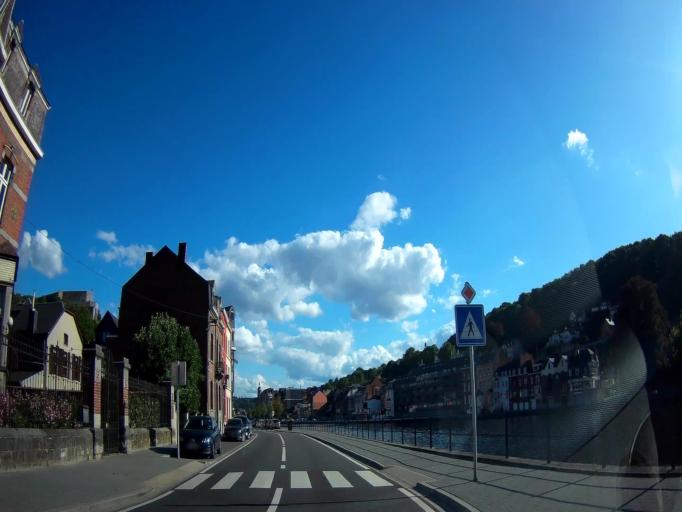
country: BE
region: Wallonia
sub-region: Province de Namur
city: Dinant
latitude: 50.2641
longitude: 4.9079
